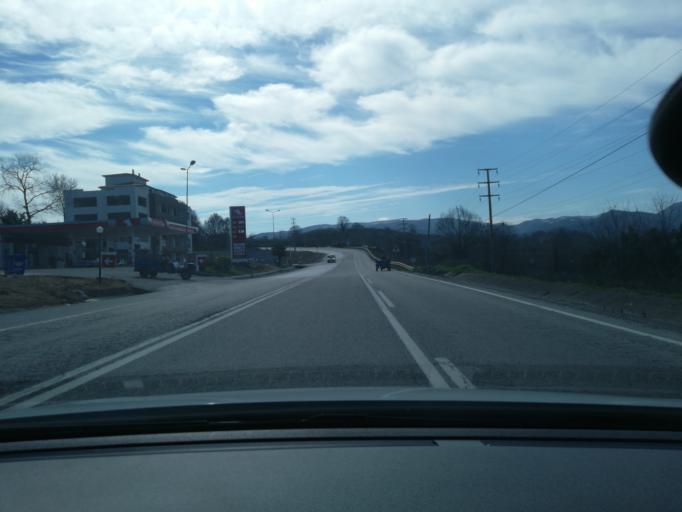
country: TR
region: Duzce
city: Akcakoca
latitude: 41.0747
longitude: 31.1087
